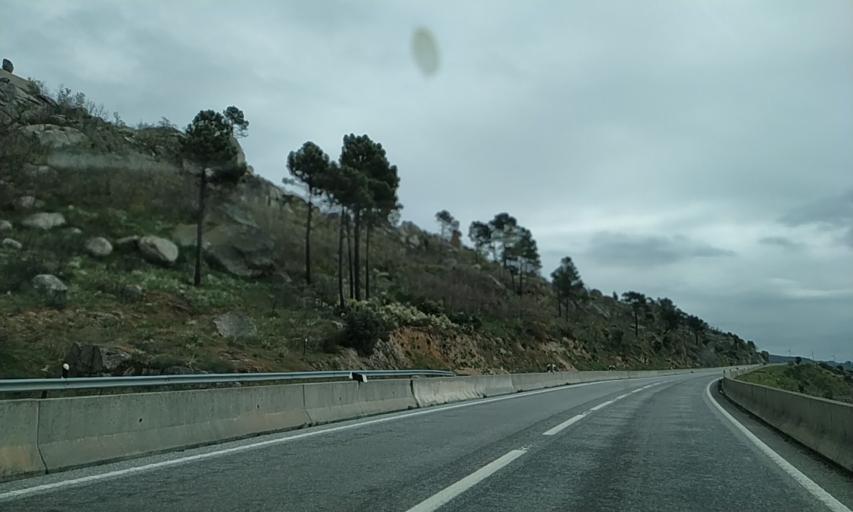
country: PT
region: Guarda
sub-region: Guarda
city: Guarda
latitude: 40.6103
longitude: -7.2832
